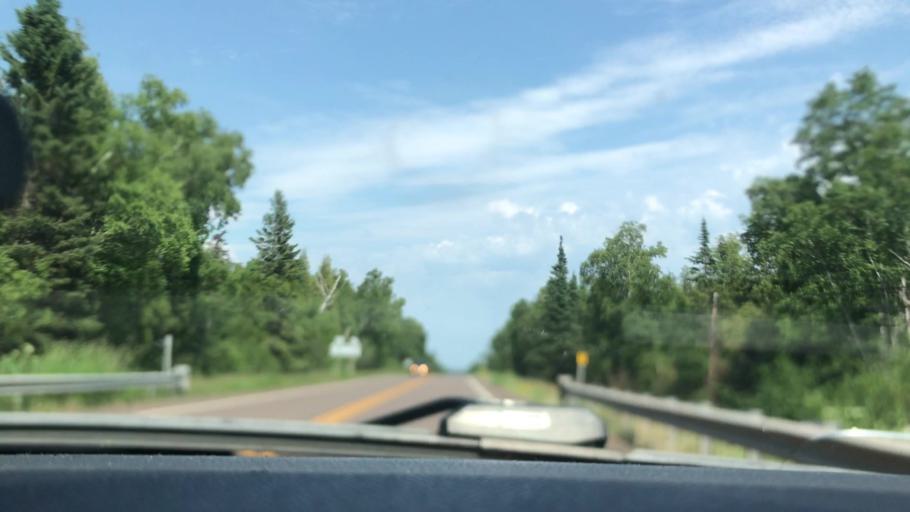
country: US
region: Minnesota
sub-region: Cook County
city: Grand Marais
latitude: 47.6405
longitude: -90.7037
